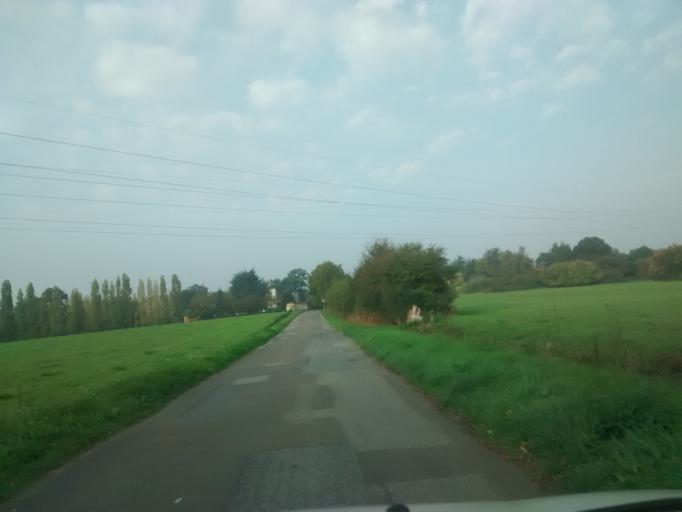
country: FR
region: Brittany
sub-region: Departement d'Ille-et-Vilaine
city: Cesson-Sevigne
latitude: 48.1309
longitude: -1.6038
